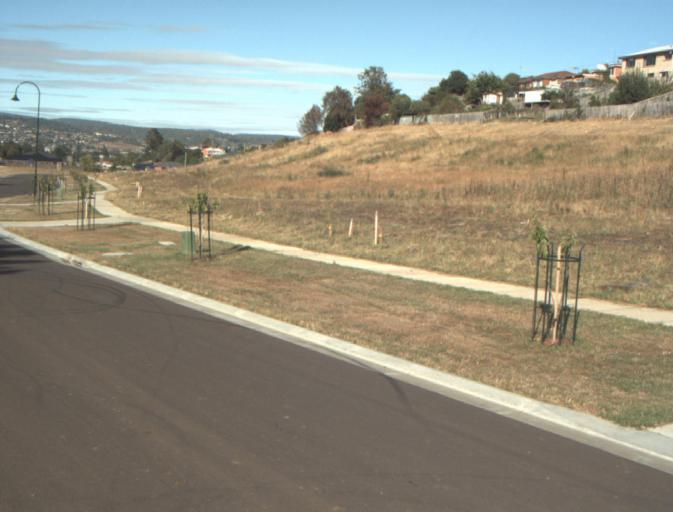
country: AU
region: Tasmania
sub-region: Launceston
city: Invermay
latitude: -41.3921
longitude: 147.1378
